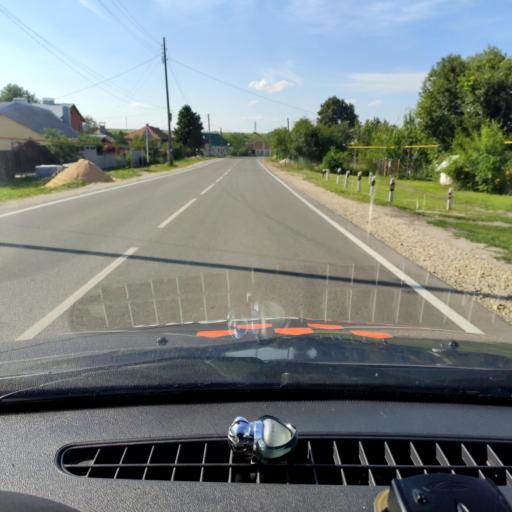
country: RU
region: Voronezj
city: Devitsa
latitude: 51.6543
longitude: 38.9713
